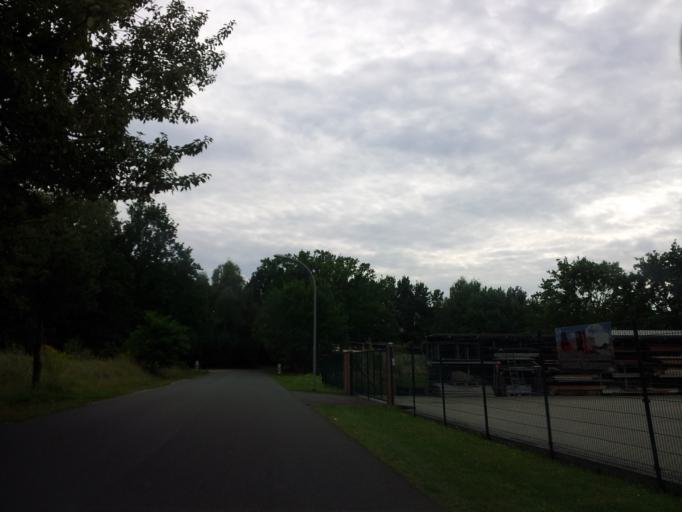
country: DE
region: Brandenburg
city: Treuenbrietzen
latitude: 52.0936
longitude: 12.8475
